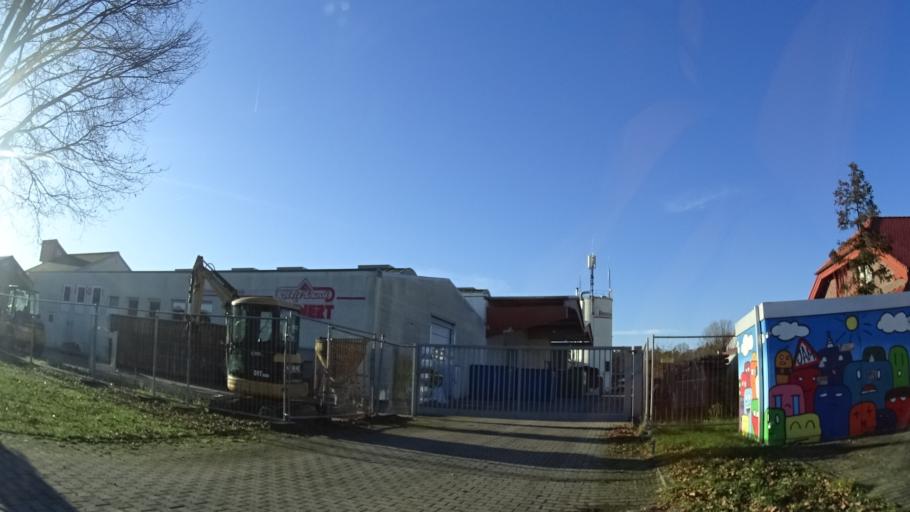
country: DE
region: Baden-Wuerttemberg
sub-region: Karlsruhe Region
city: Sankt Leon-Rot
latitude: 49.2605
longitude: 8.6095
